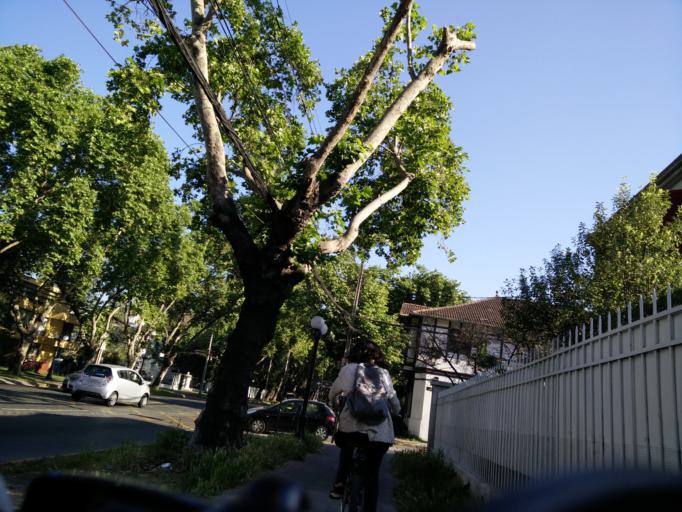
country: CL
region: Santiago Metropolitan
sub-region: Provincia de Santiago
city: Villa Presidente Frei, Nunoa, Santiago, Chile
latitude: -33.4447
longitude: -70.6061
